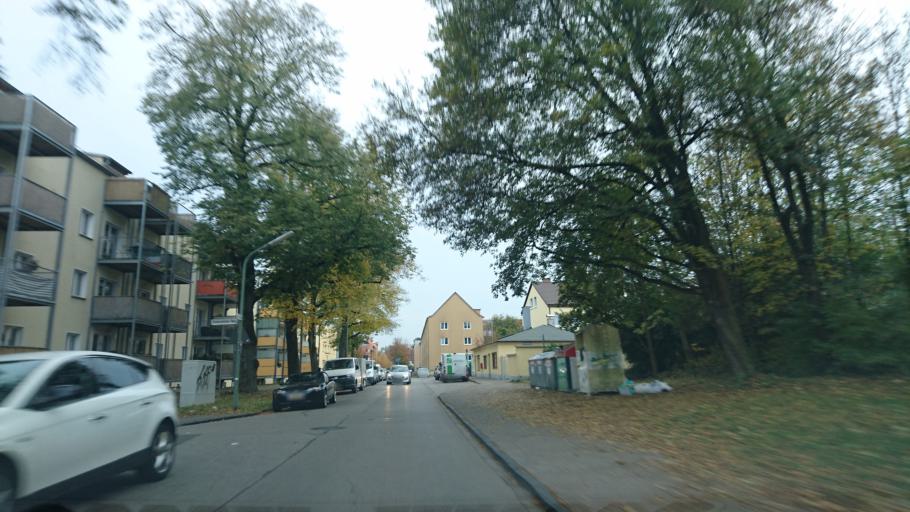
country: DE
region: Bavaria
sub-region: Swabia
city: Augsburg
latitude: 48.3943
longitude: 10.8841
